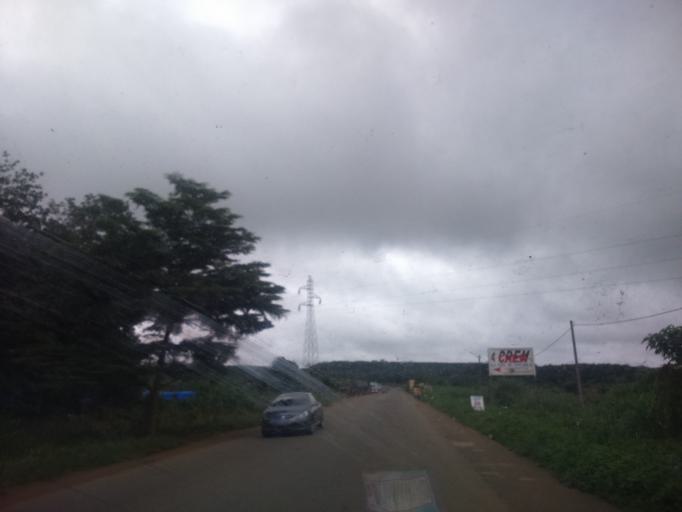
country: CI
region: Sud-Comoe
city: Bonoua
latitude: 5.2793
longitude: -3.5109
